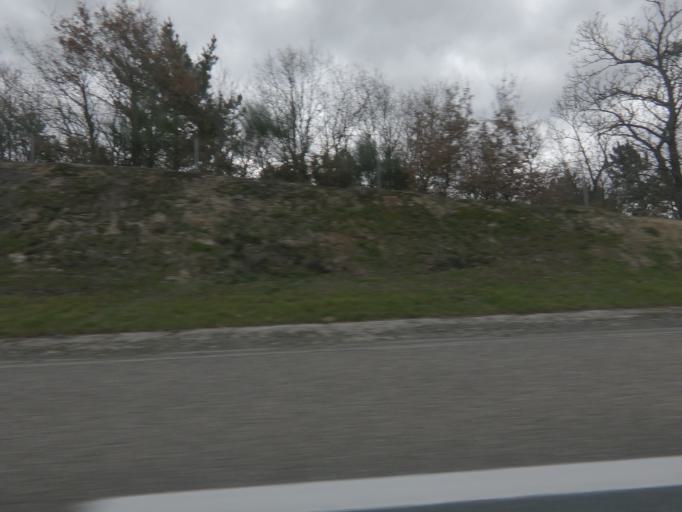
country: ES
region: Galicia
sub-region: Provincia de Ourense
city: Taboadela
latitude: 42.2341
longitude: -7.8478
